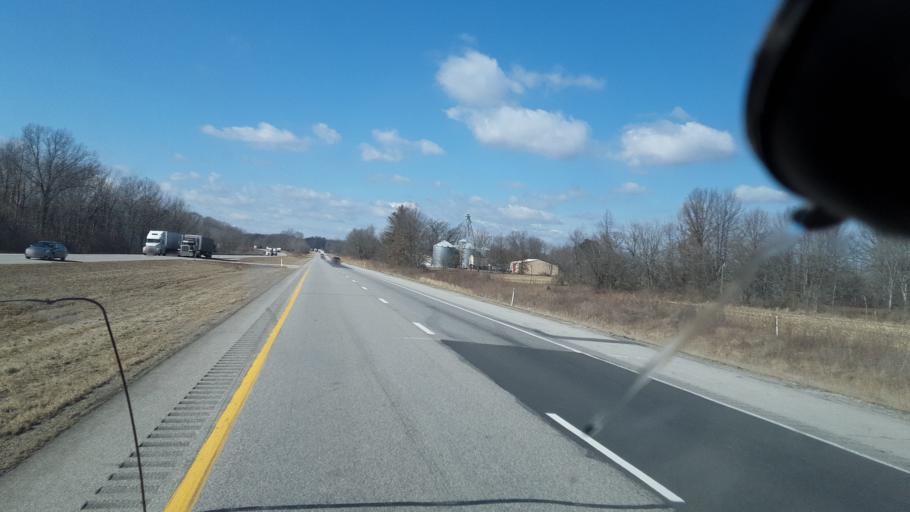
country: US
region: Indiana
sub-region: Vigo County
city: Seelyville
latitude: 39.4465
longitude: -87.2428
